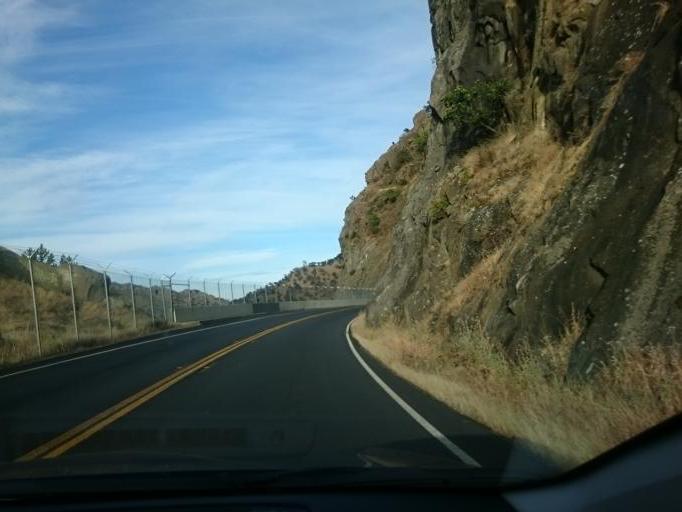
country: US
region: California
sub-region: Yolo County
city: Winters
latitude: 38.5122
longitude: -122.1061
